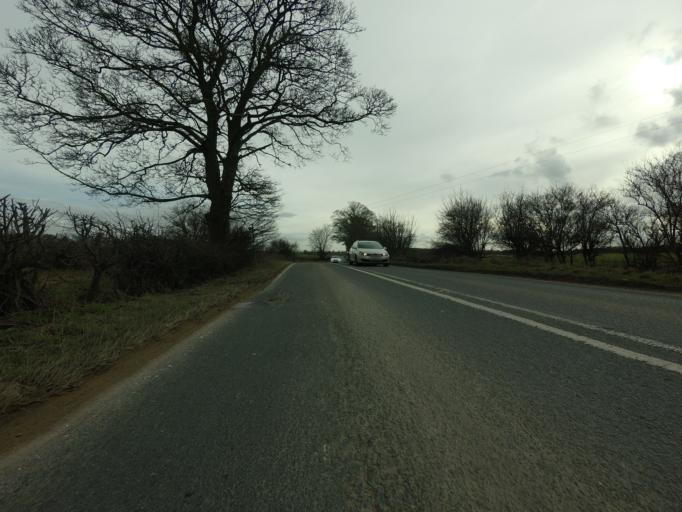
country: GB
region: England
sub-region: Lincolnshire
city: Grantham
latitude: 52.8891
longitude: -0.5951
